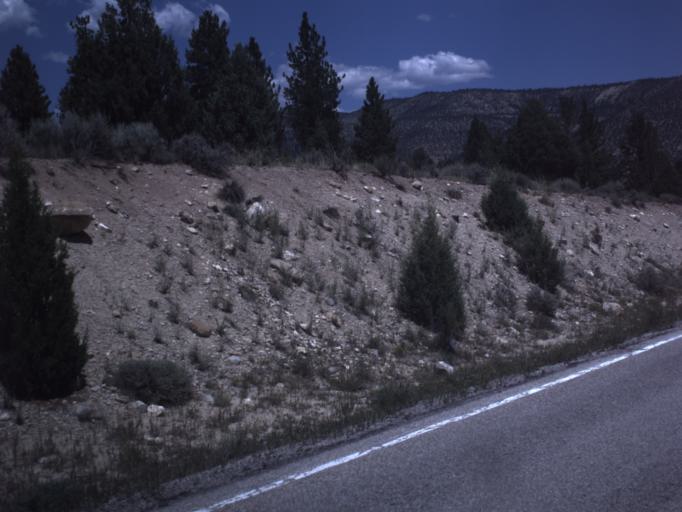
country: US
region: Utah
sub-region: Emery County
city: Orangeville
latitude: 39.2993
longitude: -111.2955
